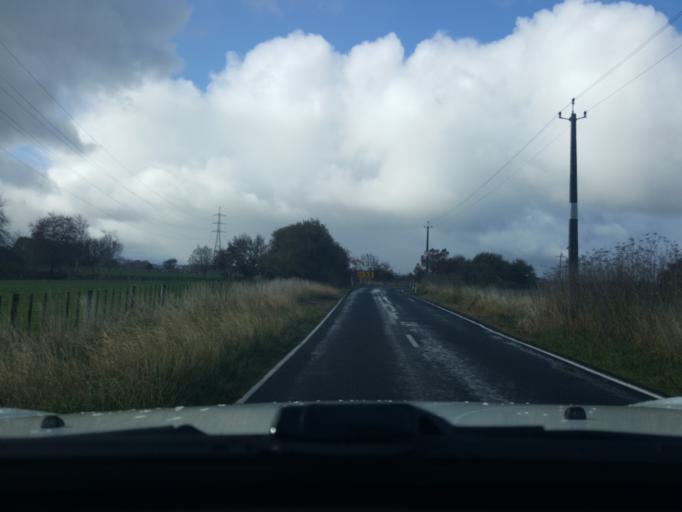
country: NZ
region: Waikato
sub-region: Waikato District
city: Te Kauwhata
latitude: -37.4475
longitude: 175.0931
